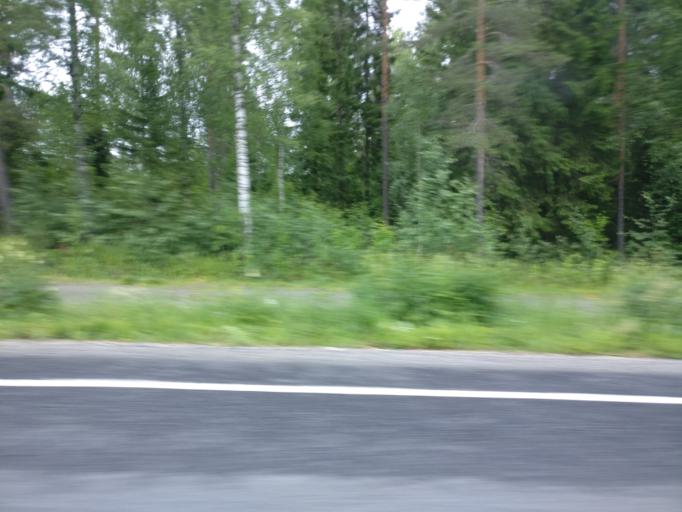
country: FI
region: Northern Savo
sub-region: Varkaus
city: Leppaevirta
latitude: 62.5853
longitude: 27.6053
